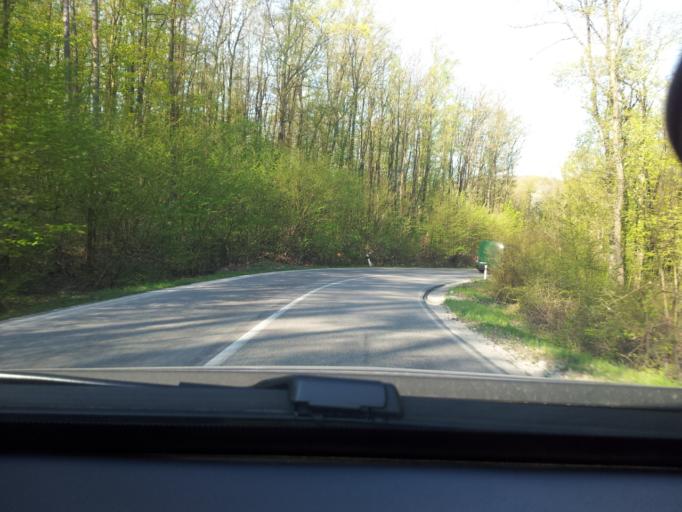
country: SK
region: Nitriansky
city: Partizanske
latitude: 48.5233
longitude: 18.3746
